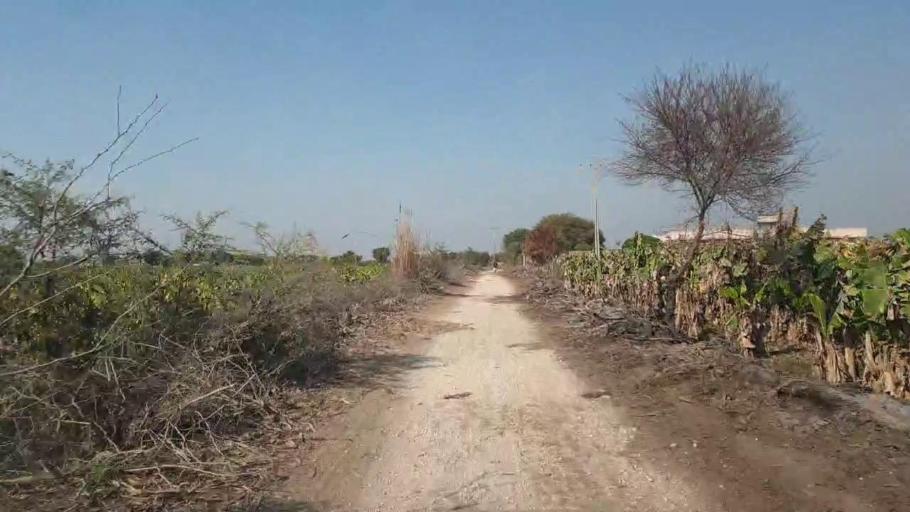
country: PK
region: Sindh
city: Chambar
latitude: 25.3243
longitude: 68.7577
